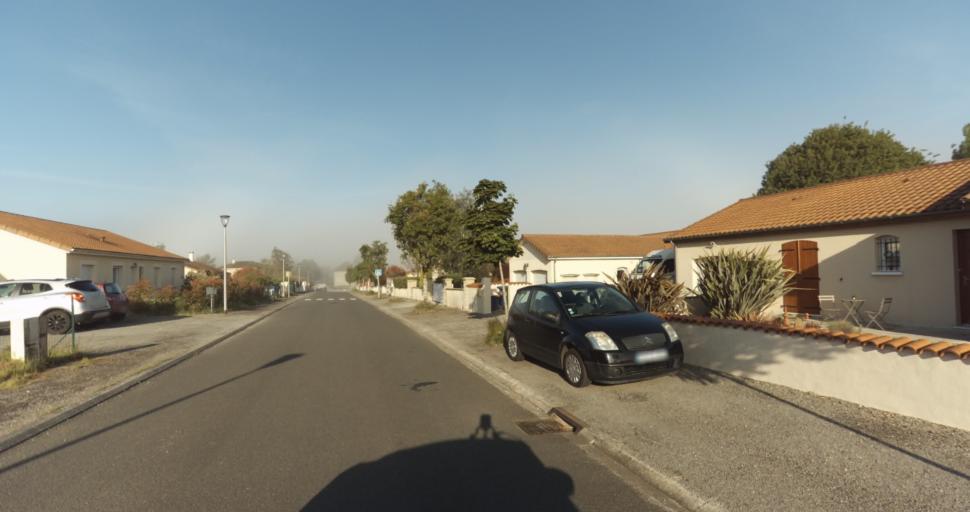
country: FR
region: Limousin
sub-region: Departement de la Haute-Vienne
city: Condat-sur-Vienne
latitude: 45.7841
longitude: 1.2852
